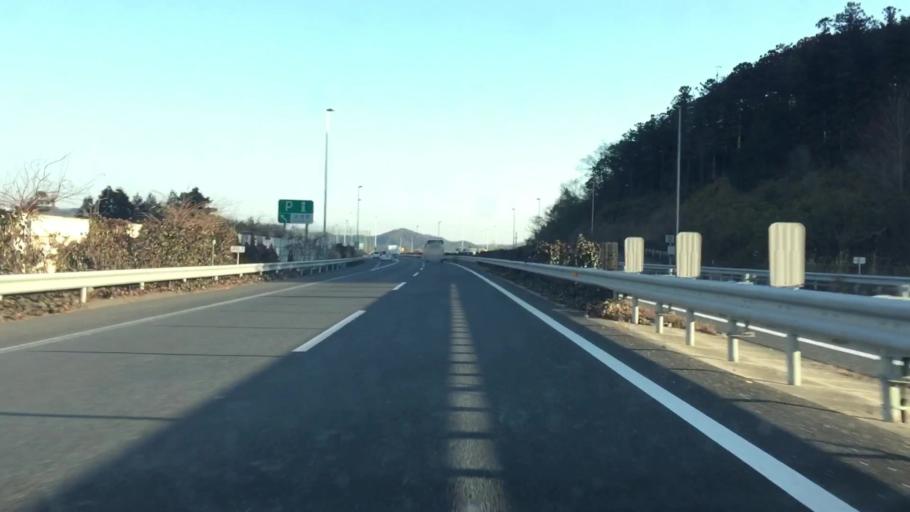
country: JP
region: Tochigi
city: Tanuma
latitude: 36.3693
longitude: 139.5439
